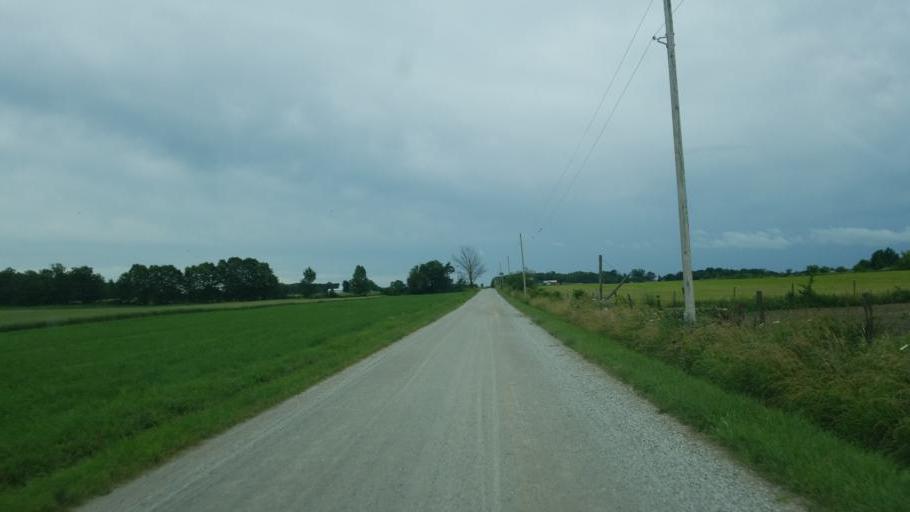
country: US
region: Ohio
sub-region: Huron County
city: Greenwich
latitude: 40.9411
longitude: -82.4312
